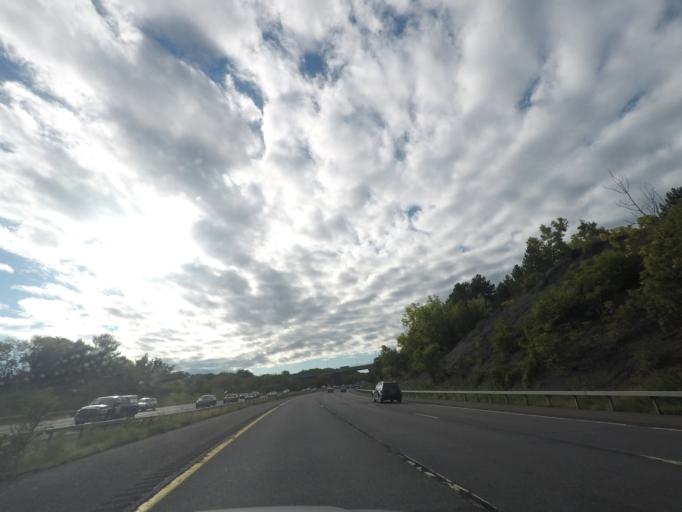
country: US
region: New York
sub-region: Albany County
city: Albany
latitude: 42.6710
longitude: -73.7504
